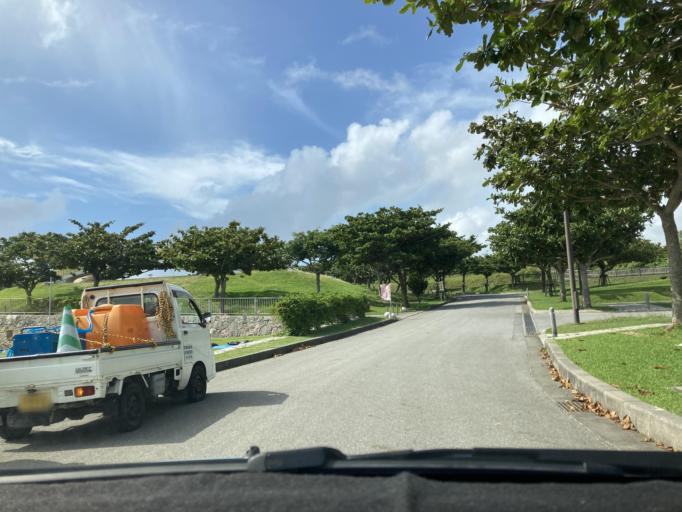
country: JP
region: Okinawa
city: Itoman
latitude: 26.0985
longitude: 127.7265
